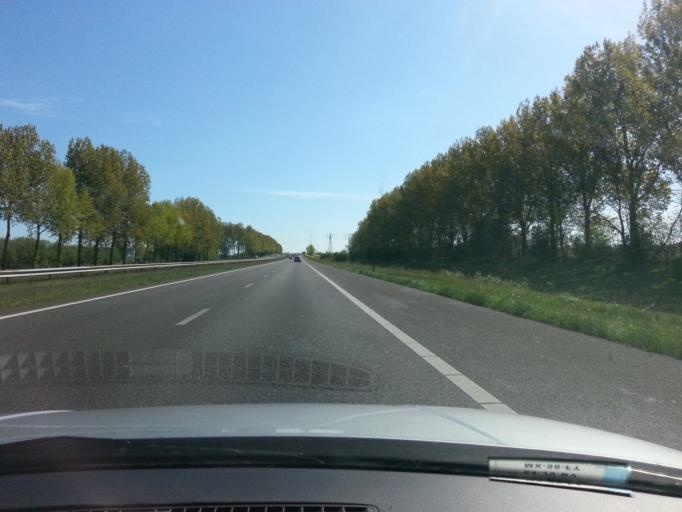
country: NL
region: Friesland
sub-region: Gemeente Skarsterlan
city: Oudehaske
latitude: 52.9656
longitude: 5.8815
